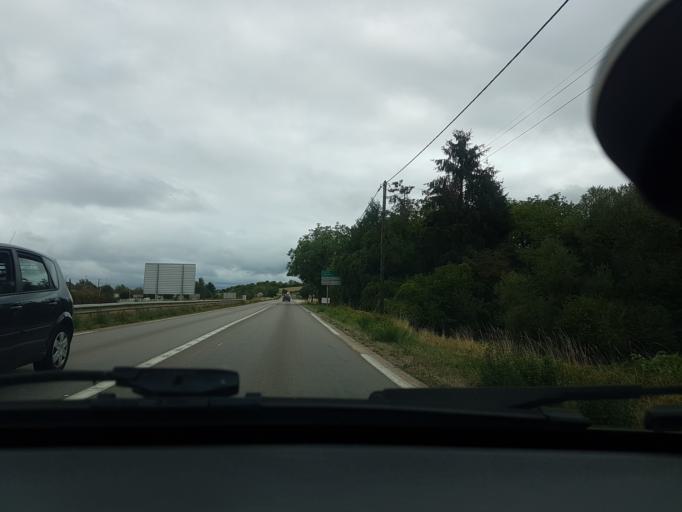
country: FR
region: Bourgogne
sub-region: Departement de l'Yonne
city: Champs-sur-Yonne
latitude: 47.7025
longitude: 3.6283
